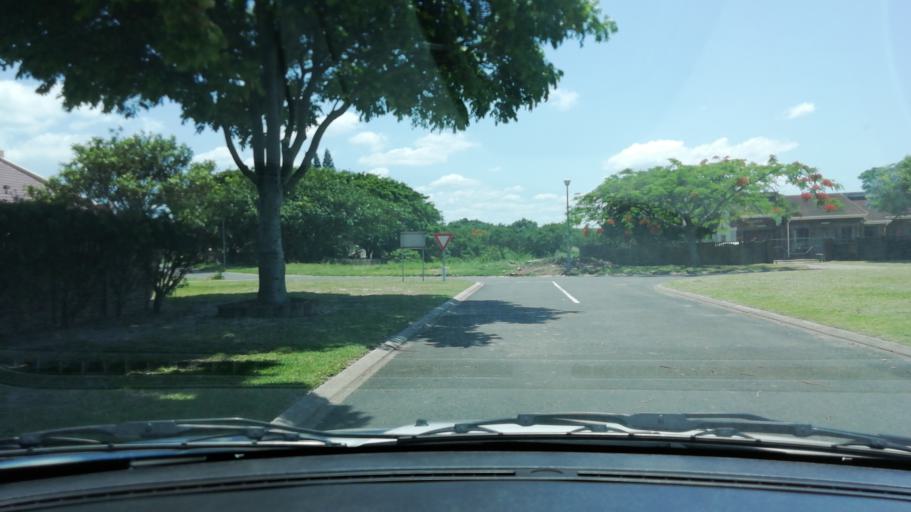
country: ZA
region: KwaZulu-Natal
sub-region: uThungulu District Municipality
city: Richards Bay
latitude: -28.7361
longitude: 32.0464
